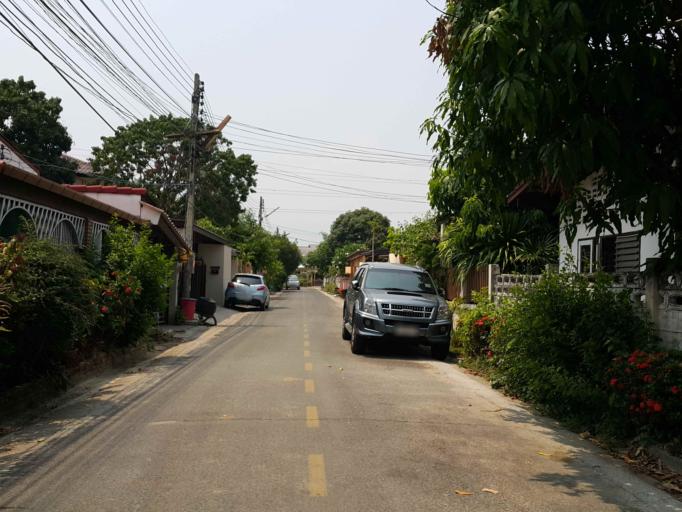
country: TH
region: Chiang Mai
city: Chiang Mai
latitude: 18.7549
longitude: 99.0114
